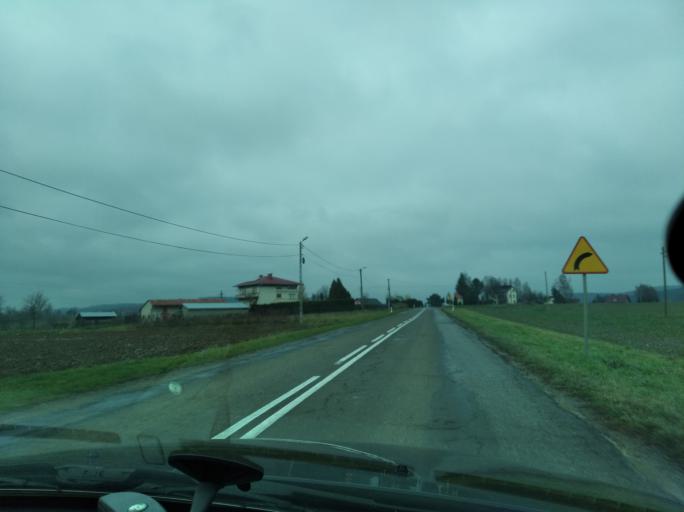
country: PL
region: Subcarpathian Voivodeship
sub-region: Powiat rzeszowski
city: Dynow
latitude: 49.8437
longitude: 22.2436
